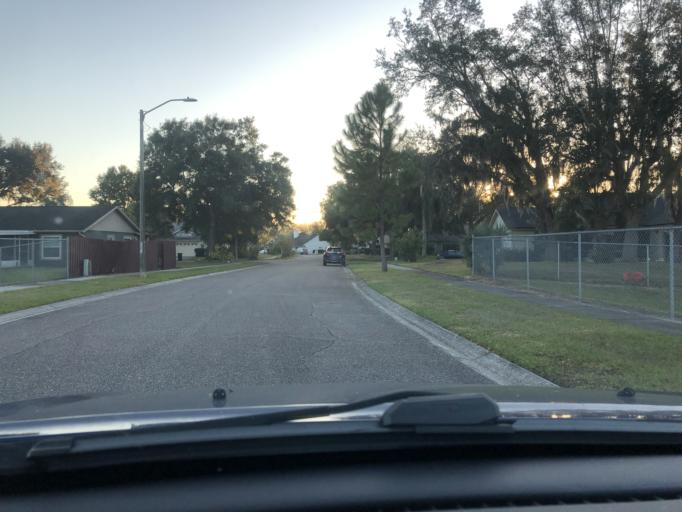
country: US
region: Florida
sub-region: Seminole County
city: Goldenrod
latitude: 28.6107
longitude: -81.2633
